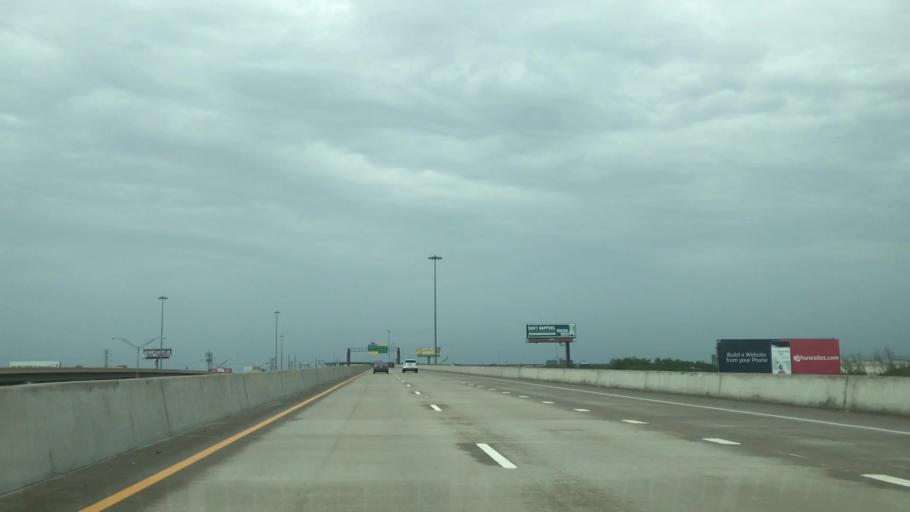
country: US
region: Texas
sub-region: Dallas County
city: Farmers Branch
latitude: 32.8897
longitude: -96.8977
